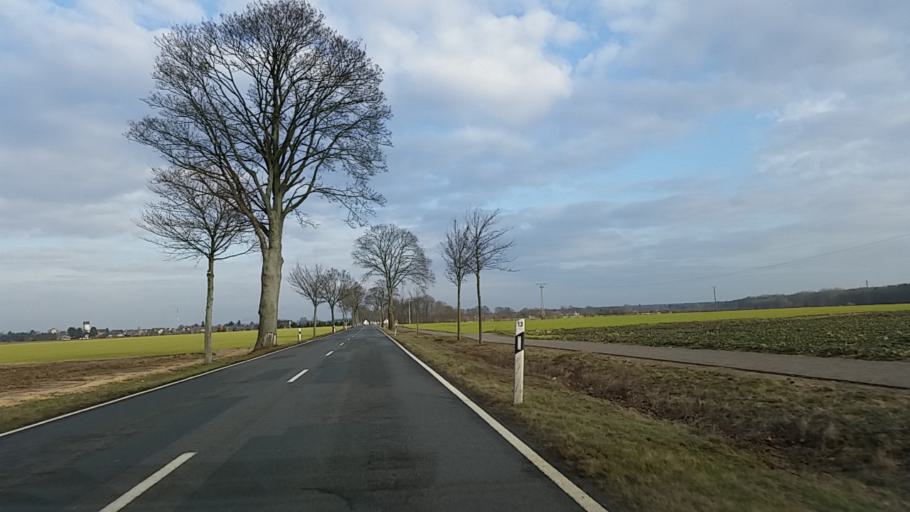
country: DE
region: Lower Saxony
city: Brome
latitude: 52.5845
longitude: 10.9320
